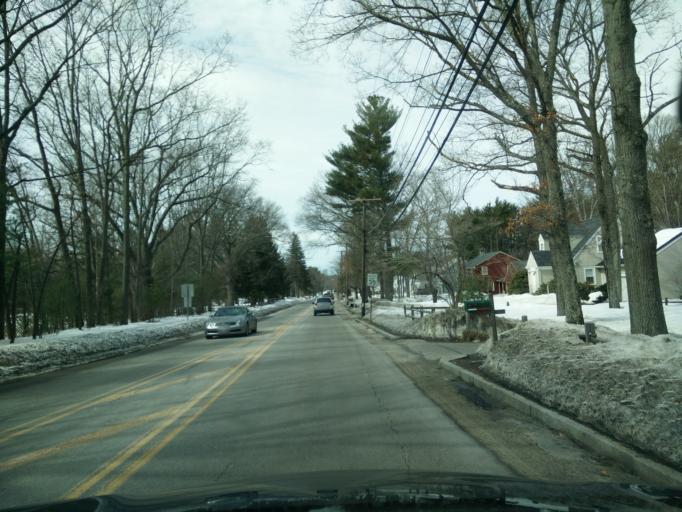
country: US
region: Massachusetts
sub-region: Norfolk County
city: Walpole
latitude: 42.1461
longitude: -71.2310
